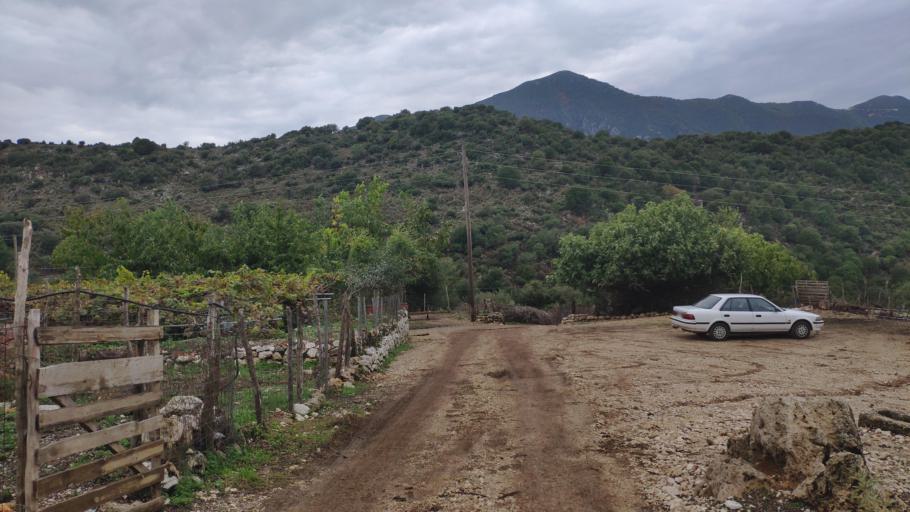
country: GR
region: Epirus
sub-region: Nomos Prevezis
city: Kanalaki
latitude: 39.3623
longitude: 20.6423
